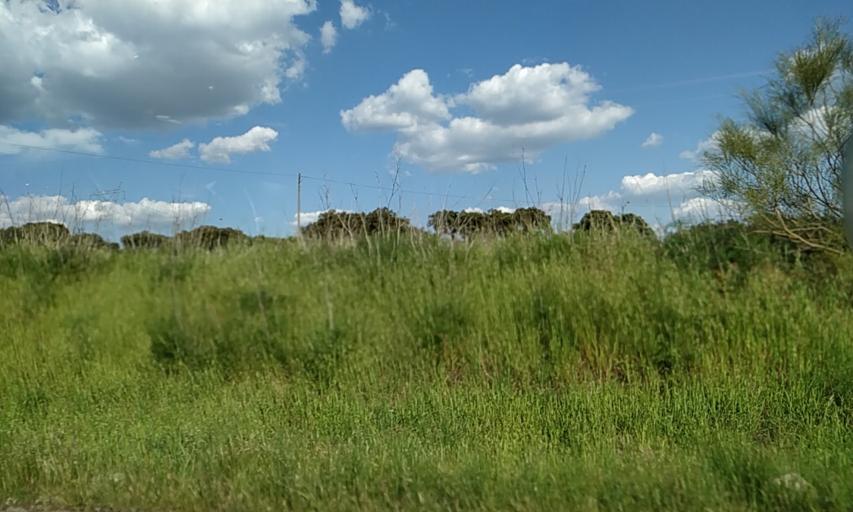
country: PT
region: Evora
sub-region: Estremoz
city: Estremoz
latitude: 38.8798
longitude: -7.5605
